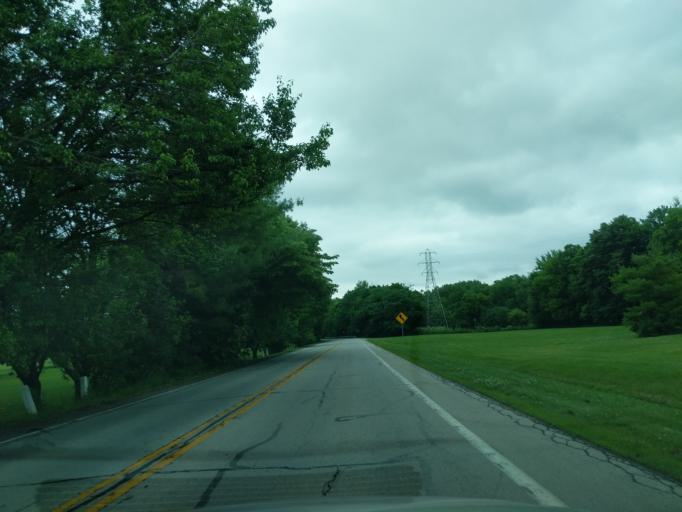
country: US
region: Indiana
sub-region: Hamilton County
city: Noblesville
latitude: 40.0508
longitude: -86.0156
